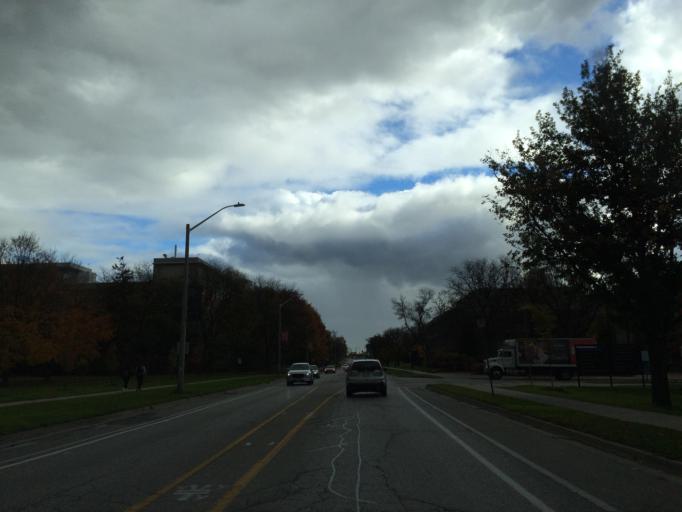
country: CA
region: Ontario
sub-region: Wellington County
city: Guelph
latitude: 43.5311
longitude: -80.2311
